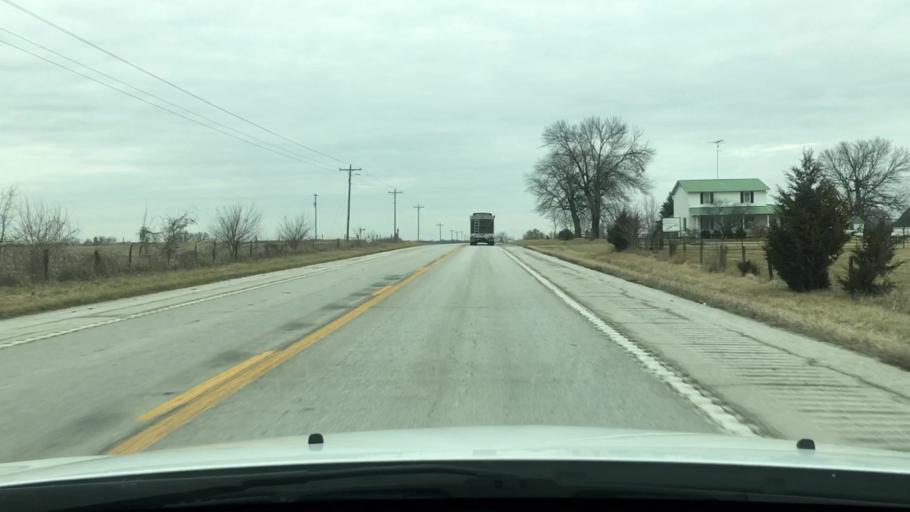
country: US
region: Missouri
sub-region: Montgomery County
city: Wellsville
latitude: 39.1761
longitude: -91.6475
